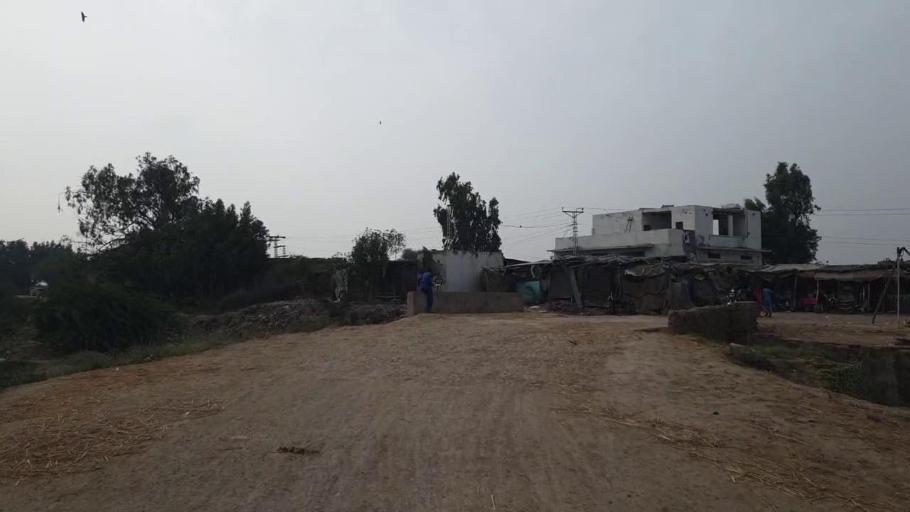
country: PK
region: Sindh
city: Kario
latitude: 24.8816
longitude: 68.5258
